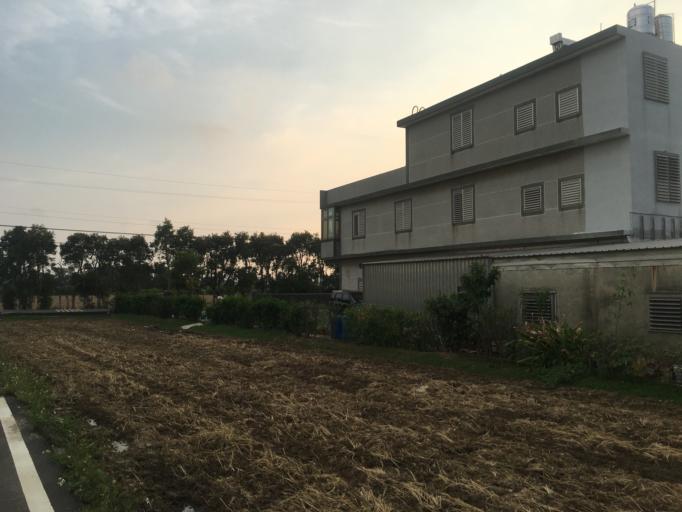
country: TW
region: Taiwan
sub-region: Hsinchu
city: Zhubei
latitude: 24.9154
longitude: 121.0075
